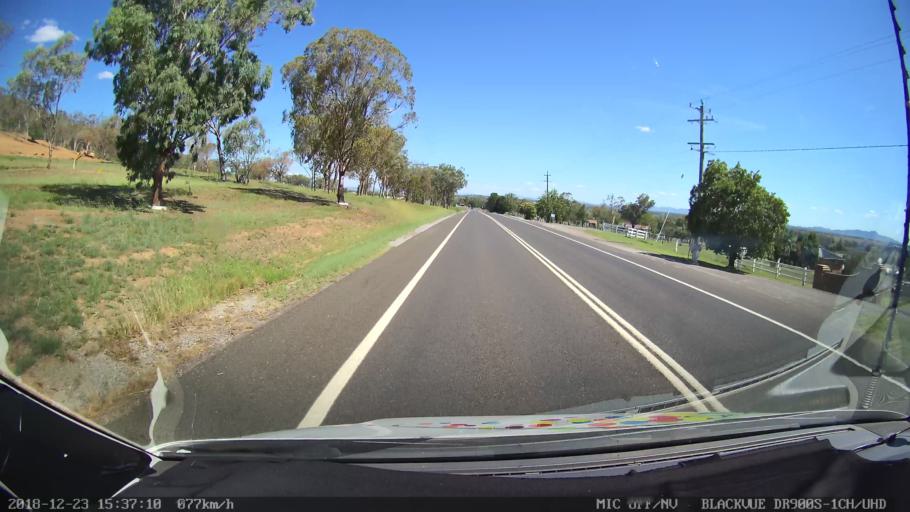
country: AU
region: New South Wales
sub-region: Tamworth Municipality
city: Tamworth
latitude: -31.0492
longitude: 150.8892
